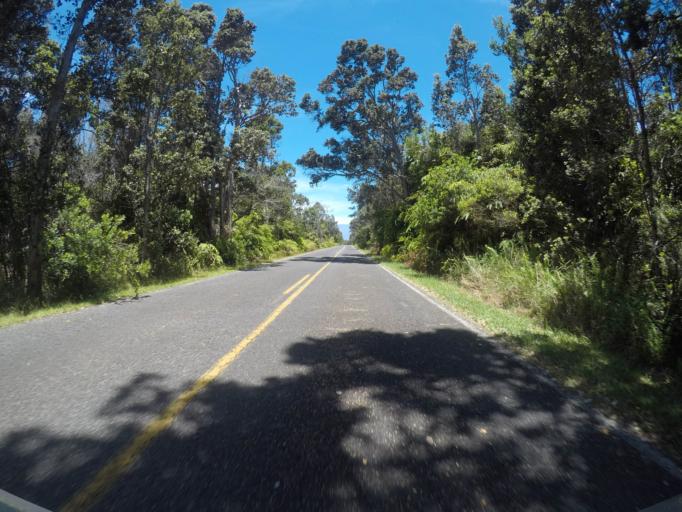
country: US
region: Hawaii
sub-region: Hawaii County
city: Volcano
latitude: 19.3655
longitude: -155.2172
